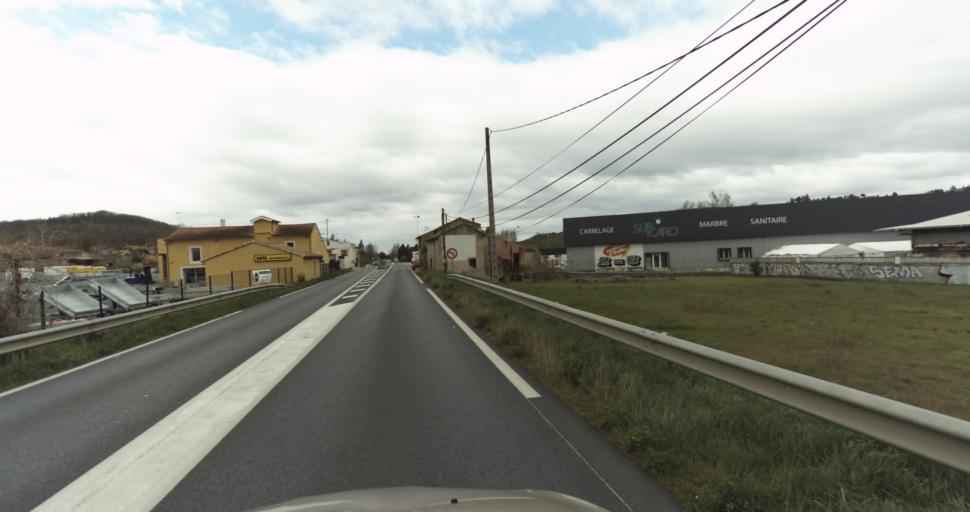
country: FR
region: Midi-Pyrenees
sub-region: Departement du Tarn
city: Puygouzon
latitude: 43.8942
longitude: 2.1541
